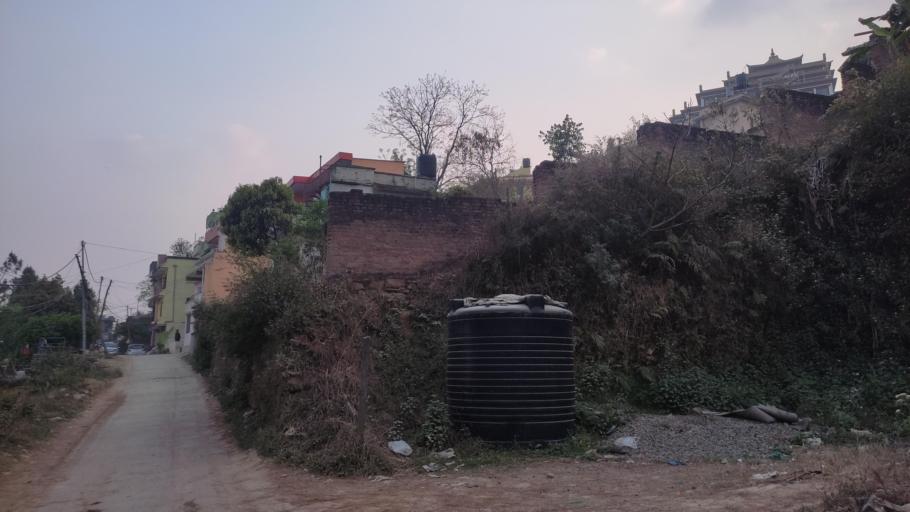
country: NP
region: Central Region
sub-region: Bagmati Zone
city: Patan
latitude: 27.6657
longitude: 85.2938
